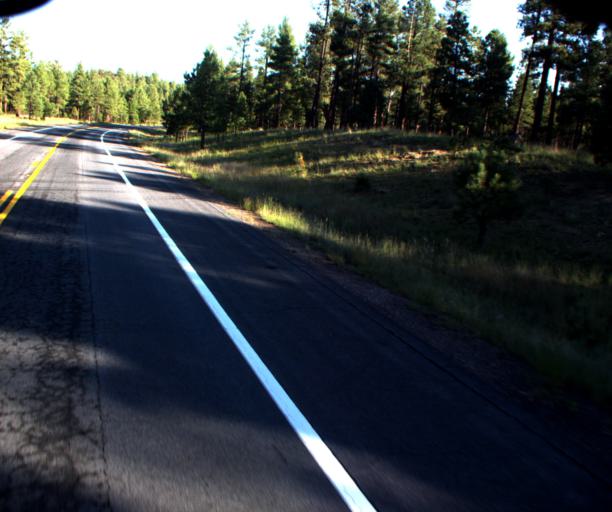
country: US
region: New Mexico
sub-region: Catron County
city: Reserve
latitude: 33.8139
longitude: -109.0711
